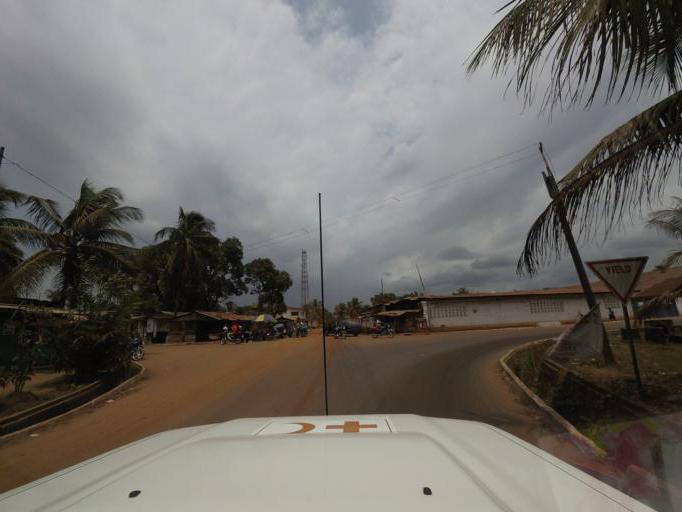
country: LR
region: Montserrado
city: Monrovia
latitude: 6.3028
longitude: -10.6864
